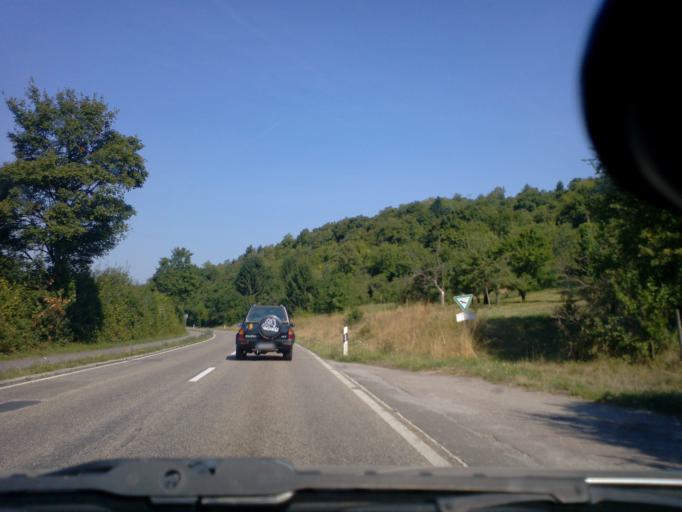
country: DE
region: Baden-Wuerttemberg
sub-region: Karlsruhe Region
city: Joehlingen
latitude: 49.0807
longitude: 8.5683
